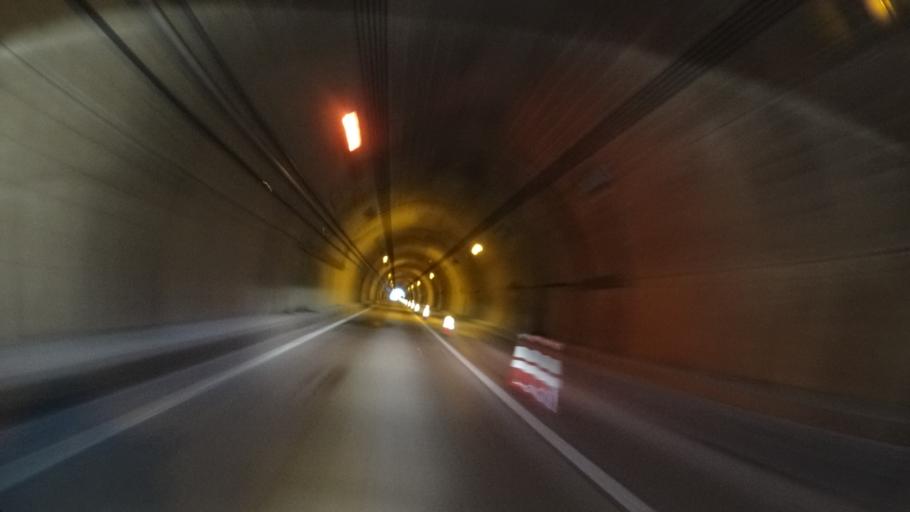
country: JP
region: Fukui
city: Maruoka
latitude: 36.1214
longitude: 136.3175
